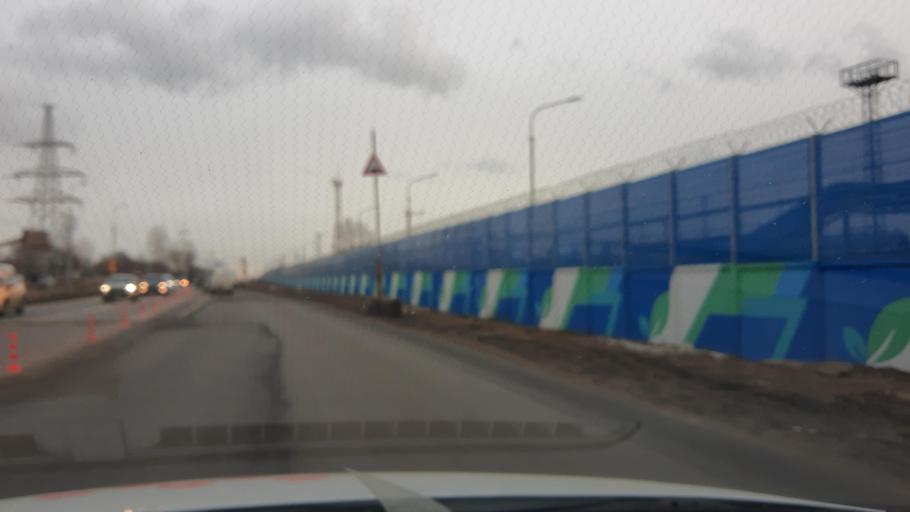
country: RU
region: Moscow
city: Kapotnya
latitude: 55.6566
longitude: 37.7989
